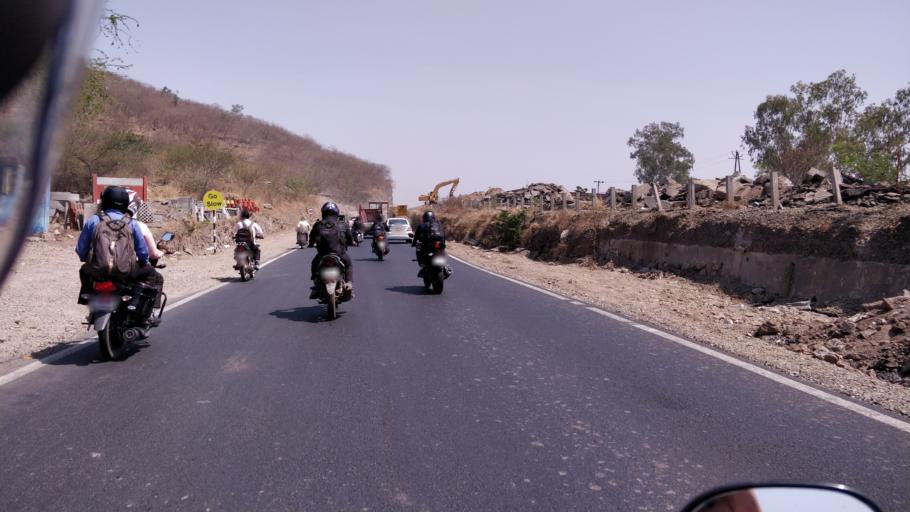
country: IN
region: Maharashtra
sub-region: Pune Division
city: Shivaji Nagar
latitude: 18.5336
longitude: 73.7799
